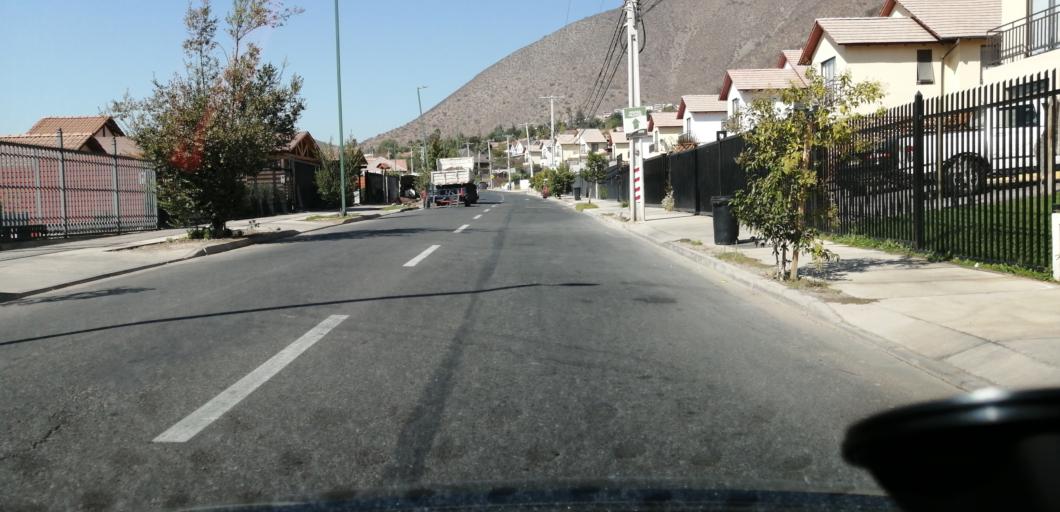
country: CL
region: Santiago Metropolitan
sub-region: Provincia de Santiago
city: Lo Prado
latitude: -33.4499
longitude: -70.8241
